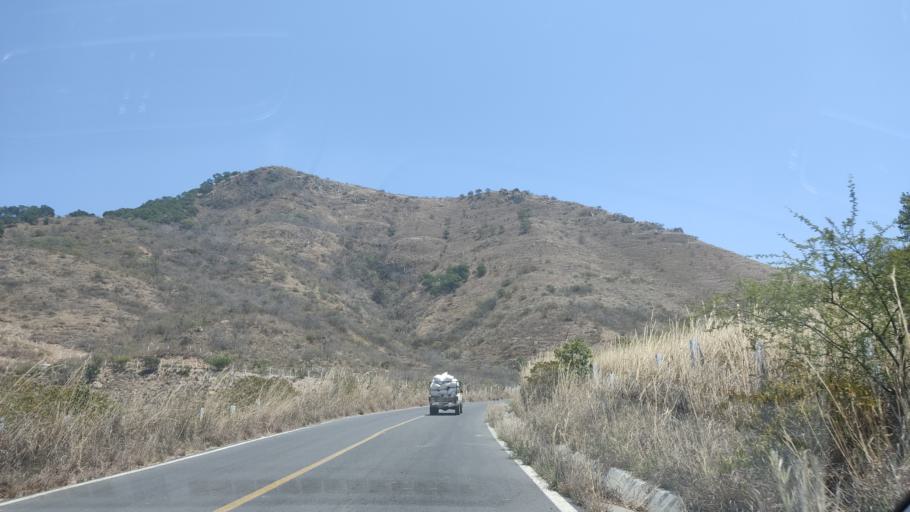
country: MX
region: Nayarit
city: Puga
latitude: 21.6129
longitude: -104.7170
